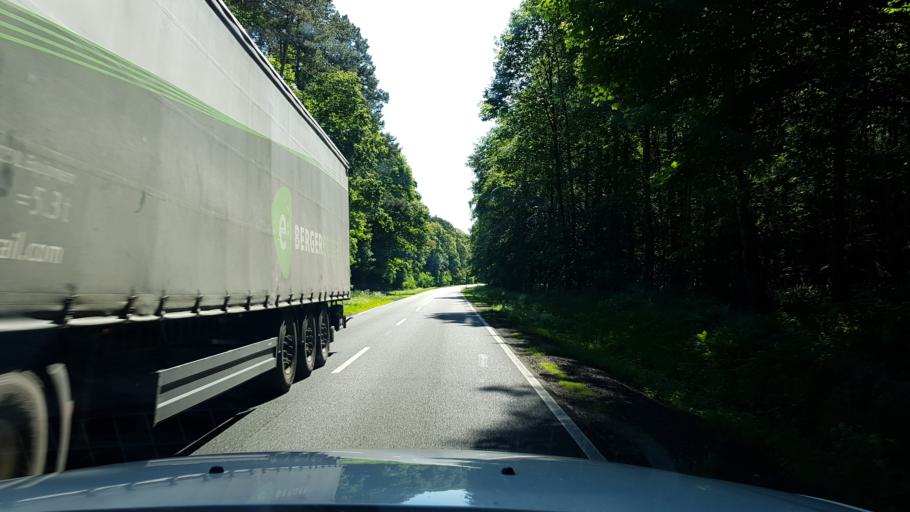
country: PL
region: West Pomeranian Voivodeship
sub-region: Powiat mysliborski
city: Boleszkowice
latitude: 52.7053
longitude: 14.5940
